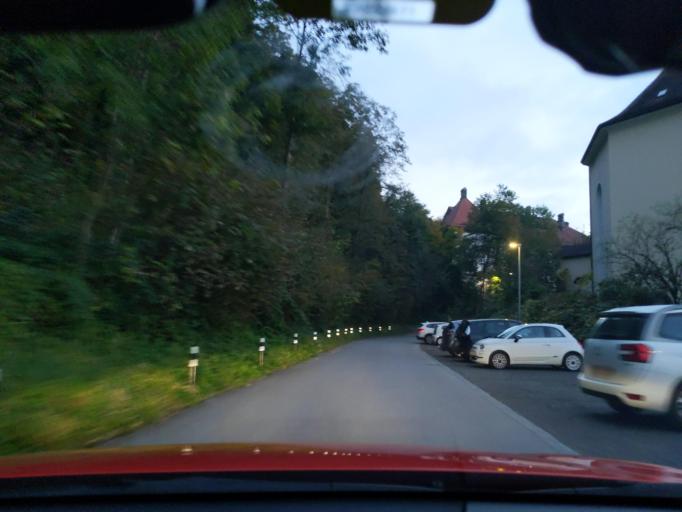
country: AT
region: Vorarlberg
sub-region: Politischer Bezirk Dornbirn
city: Hohenems
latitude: 47.3640
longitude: 9.6910
